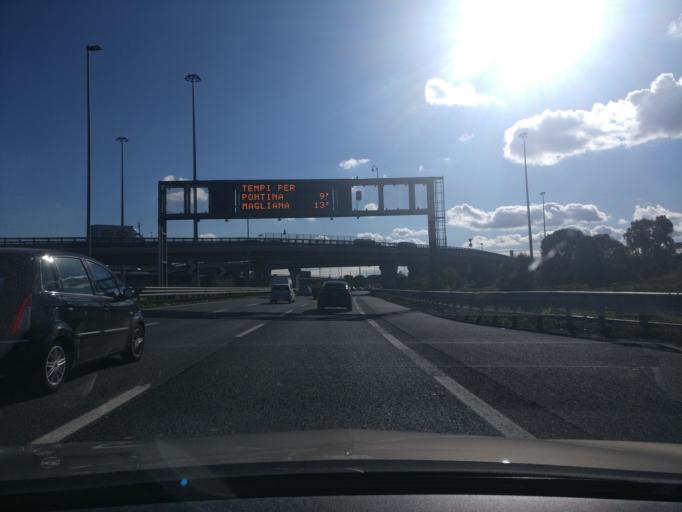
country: IT
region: Latium
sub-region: Citta metropolitana di Roma Capitale
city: Ciampino
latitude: 41.8245
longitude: 12.5807
